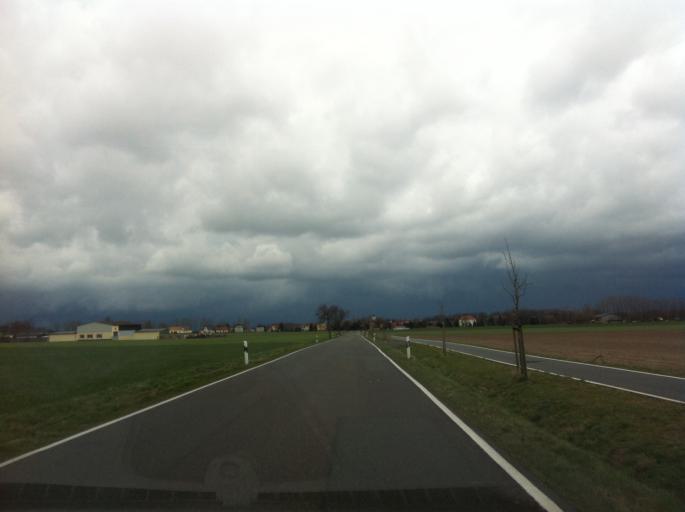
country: DE
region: Saxony
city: Doberschutz
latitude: 51.4478
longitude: 12.7642
